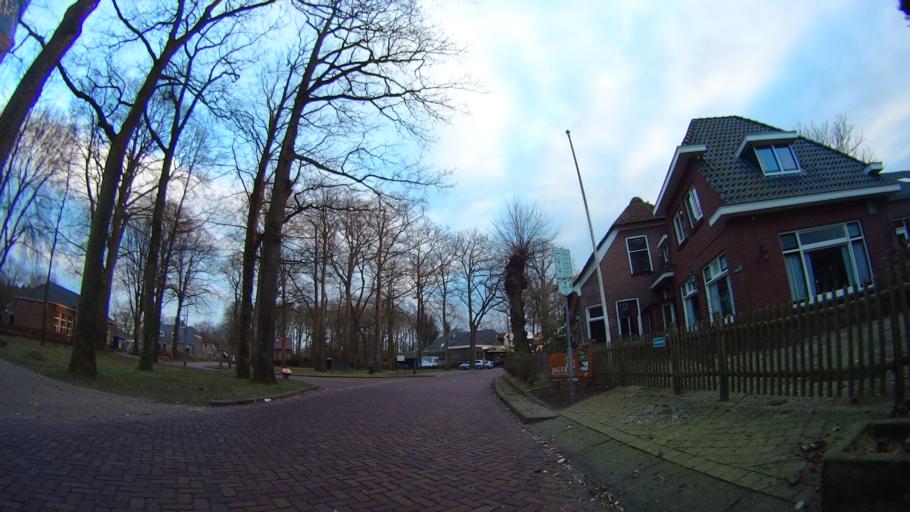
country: NL
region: Drenthe
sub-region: Gemeente Coevorden
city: Sleen
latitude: 52.7759
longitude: 6.8017
